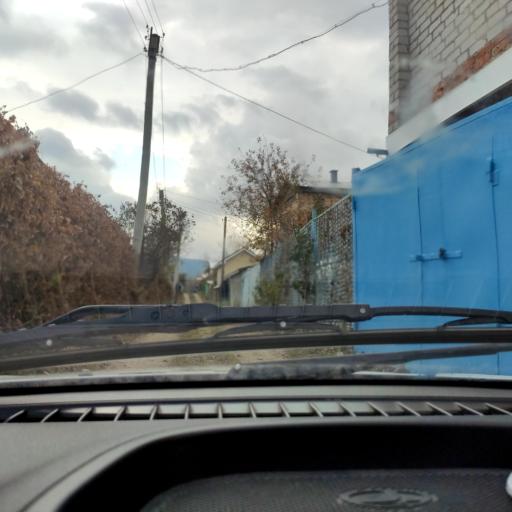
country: RU
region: Samara
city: Zhigulevsk
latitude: 53.4646
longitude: 49.6428
